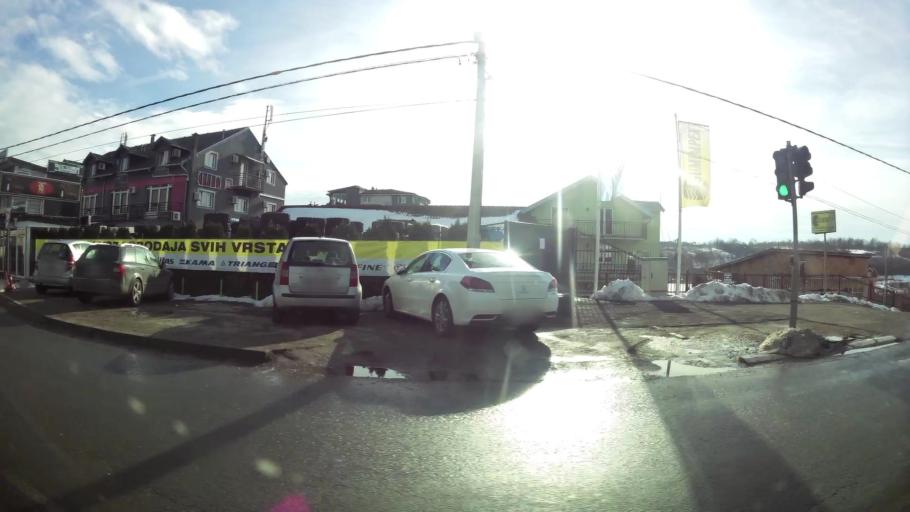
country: RS
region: Central Serbia
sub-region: Belgrade
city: Rakovica
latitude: 44.7176
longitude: 20.4237
